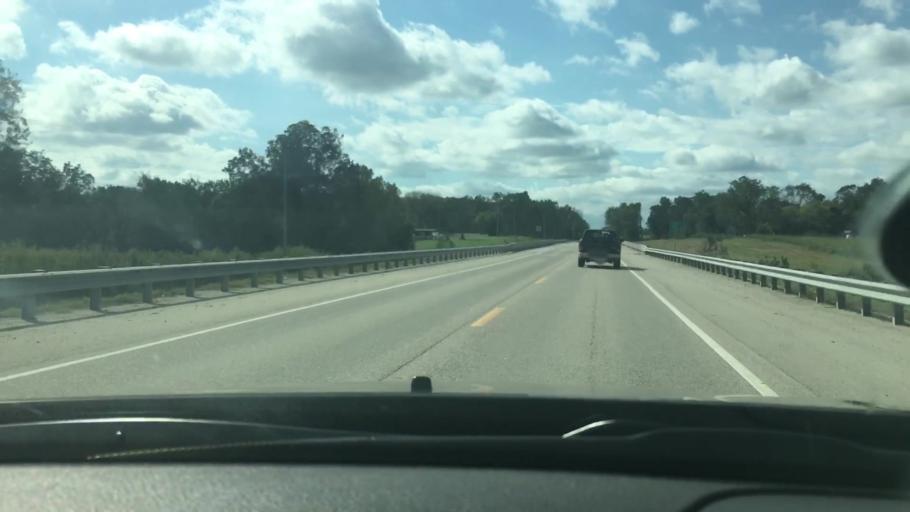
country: US
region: Oklahoma
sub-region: Pontotoc County
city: Ada
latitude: 34.7045
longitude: -96.6351
